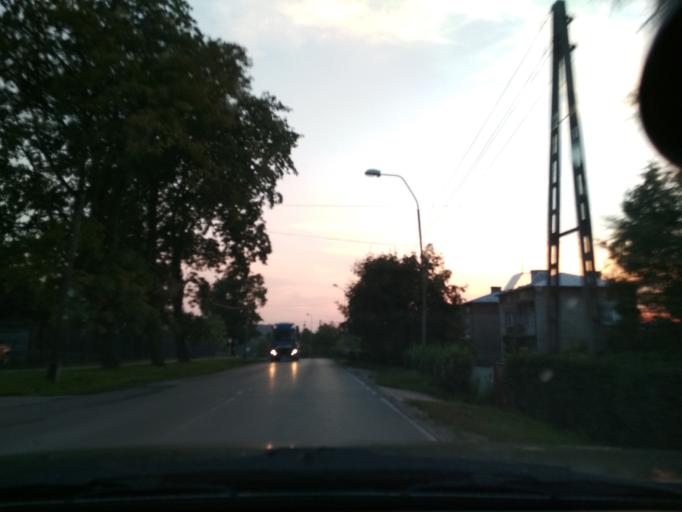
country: PL
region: Silesian Voivodeship
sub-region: Powiat zawiercianski
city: Pilica
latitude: 50.4698
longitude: 19.6697
